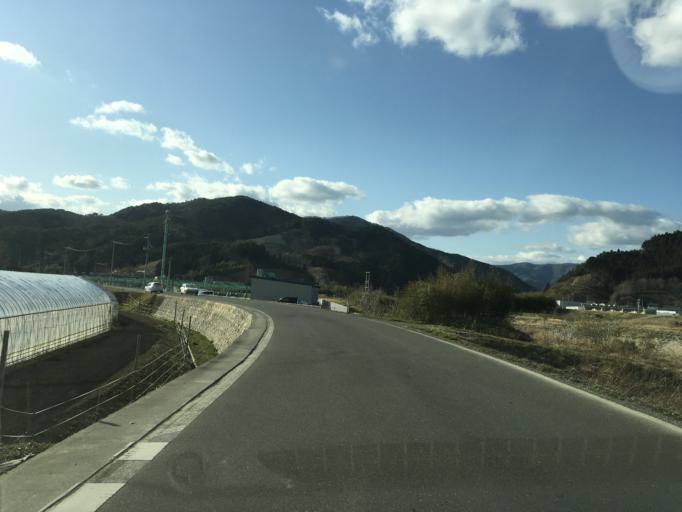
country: JP
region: Iwate
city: Ofunato
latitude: 39.0302
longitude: 141.6069
